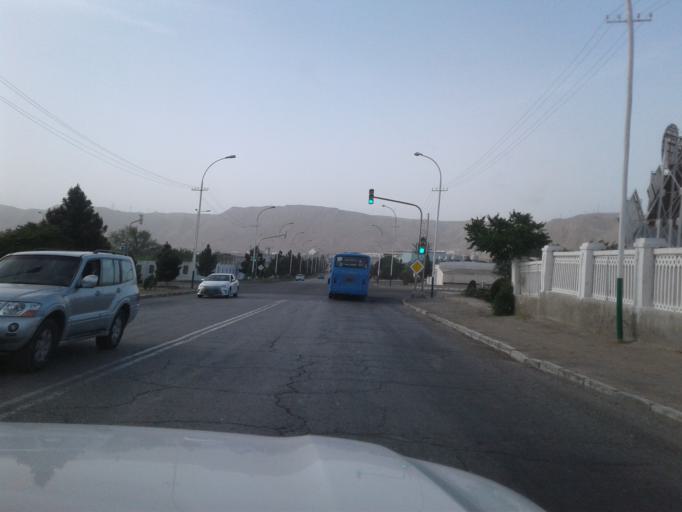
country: TM
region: Balkan
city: Turkmenbasy
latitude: 40.0220
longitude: 52.9694
